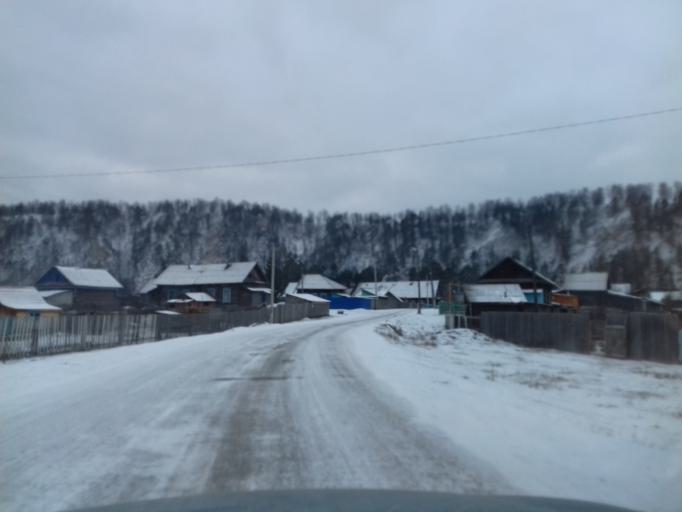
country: RU
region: Bashkortostan
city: Starosubkhangulovo
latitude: 53.0916
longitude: 57.4252
